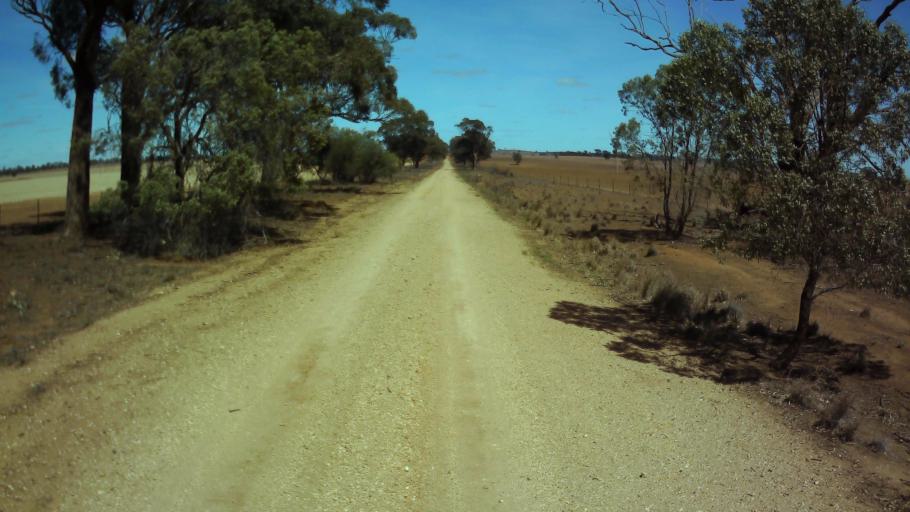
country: AU
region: New South Wales
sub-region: Weddin
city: Grenfell
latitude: -33.7264
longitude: 147.8772
